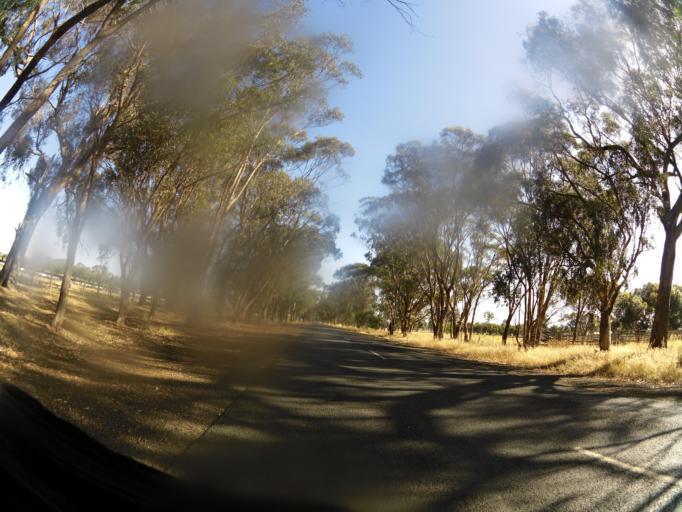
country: AU
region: Victoria
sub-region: Murrindindi
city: Kinglake West
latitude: -36.9713
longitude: 145.1094
